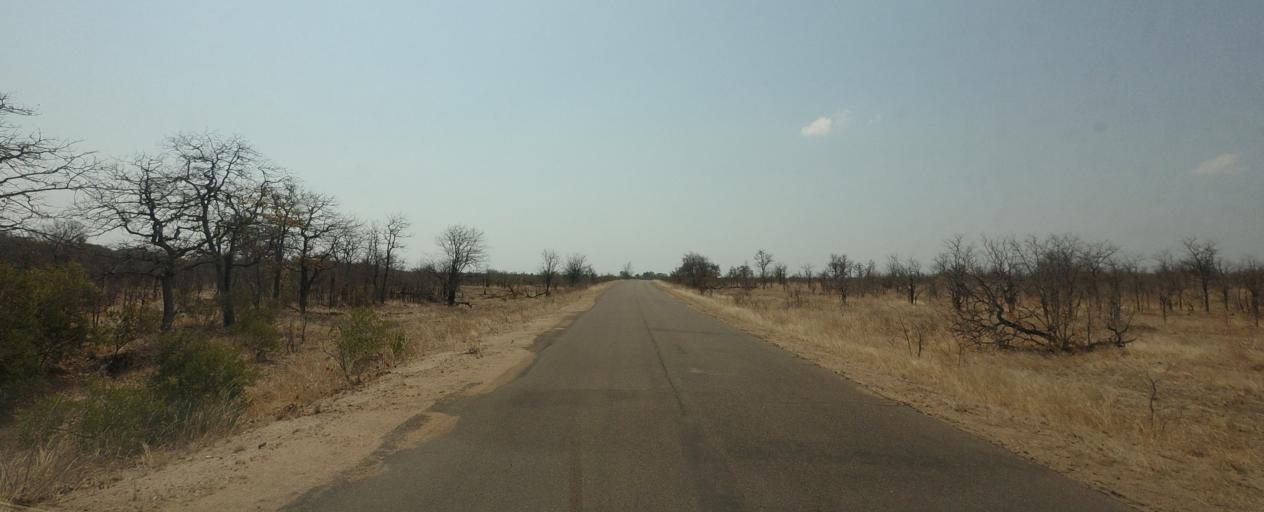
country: ZA
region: Limpopo
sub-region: Mopani District Municipality
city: Phalaborwa
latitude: -23.3778
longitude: 31.3233
